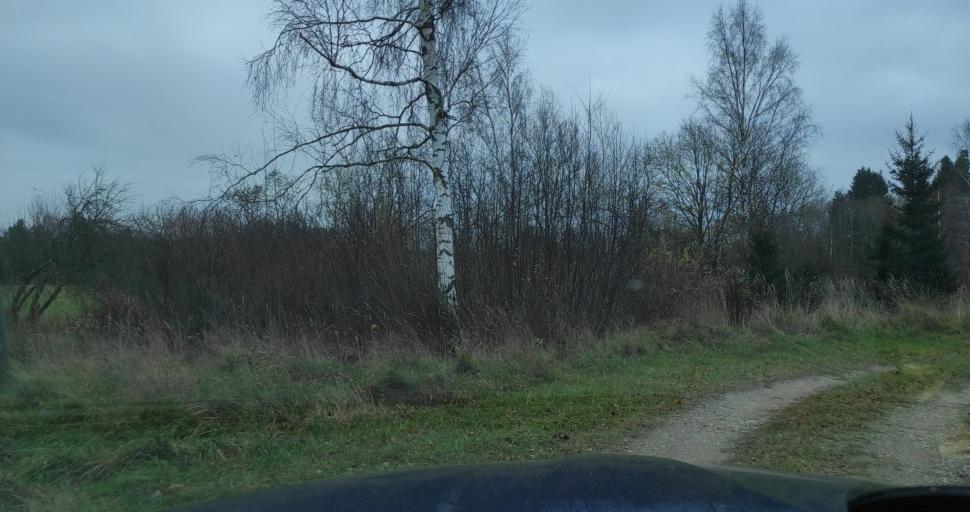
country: LV
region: Kuldigas Rajons
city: Kuldiga
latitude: 56.9973
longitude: 21.9512
